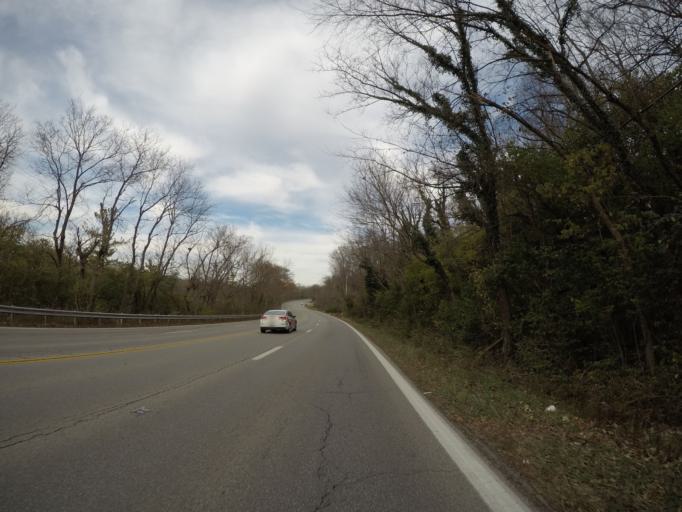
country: US
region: Ohio
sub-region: Franklin County
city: Upper Arlington
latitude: 40.0115
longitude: -83.0880
